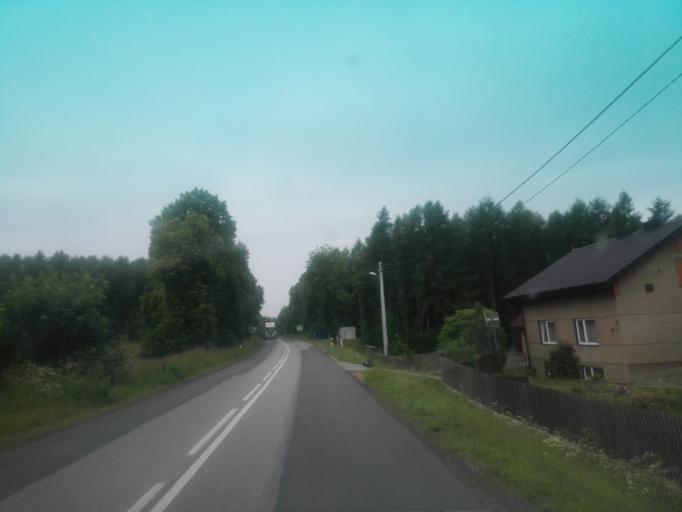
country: PL
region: Silesian Voivodeship
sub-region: Powiat czestochowski
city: Olsztyn
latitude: 50.7525
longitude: 19.2892
